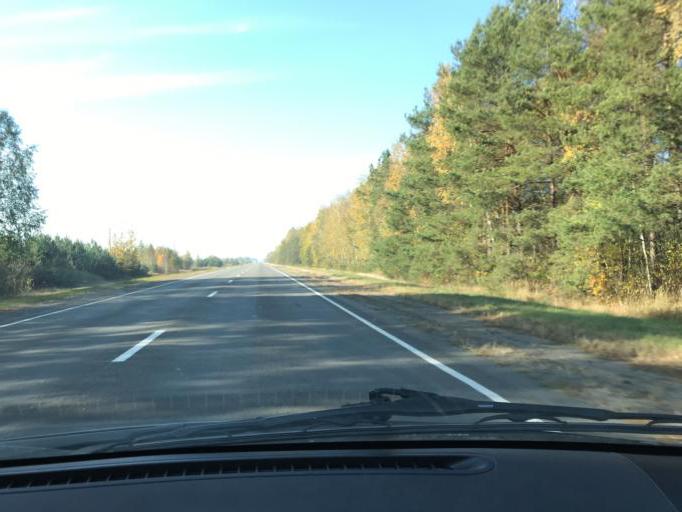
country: BY
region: Brest
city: Horad Luninyets
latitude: 52.3114
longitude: 26.5388
